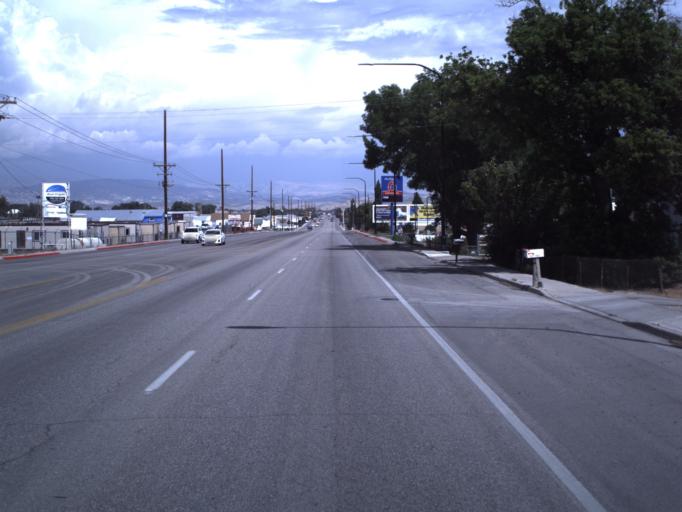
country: US
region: Utah
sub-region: Uintah County
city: Naples
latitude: 40.4263
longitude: -109.4993
